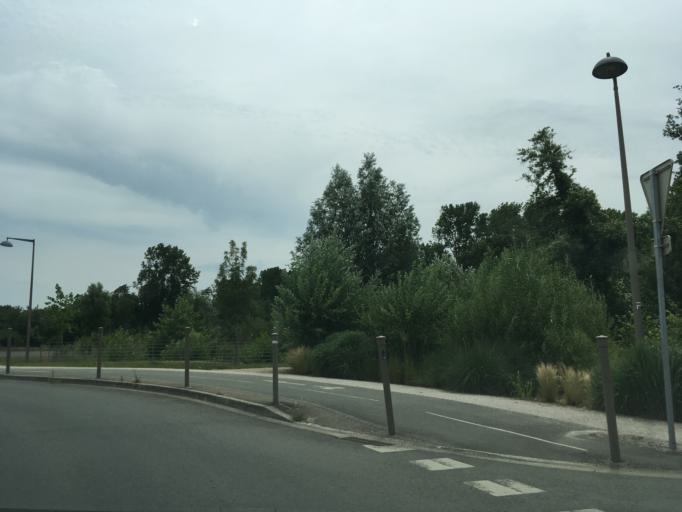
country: FR
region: Poitou-Charentes
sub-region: Departement des Deux-Sevres
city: Niort
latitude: 46.3270
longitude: -0.4905
